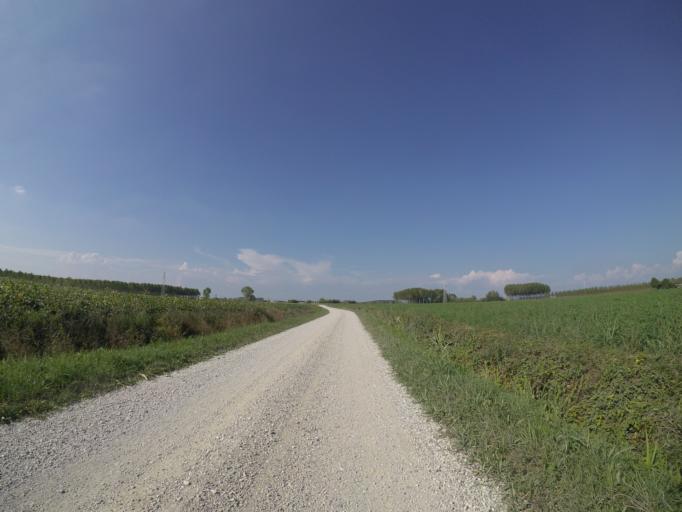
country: IT
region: Friuli Venezia Giulia
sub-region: Provincia di Udine
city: Muzzana del Turgnano
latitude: 45.8201
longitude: 13.1177
